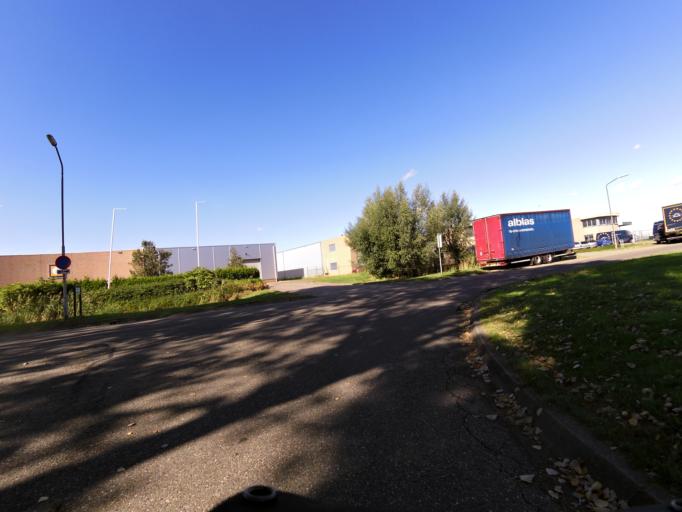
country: NL
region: South Holland
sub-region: Gemeente Zwijndrecht
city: Zwijndrecht
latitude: 51.7882
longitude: 4.6116
